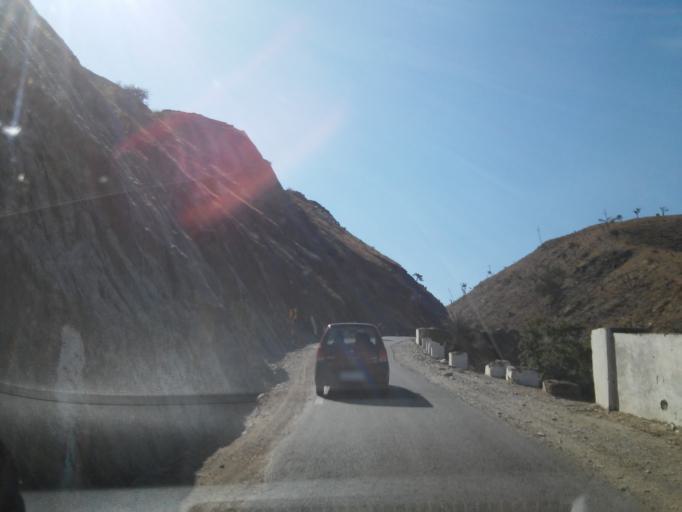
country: IN
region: Rajasthan
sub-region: Udaipur
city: Udaipur
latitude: 24.4962
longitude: 73.5953
